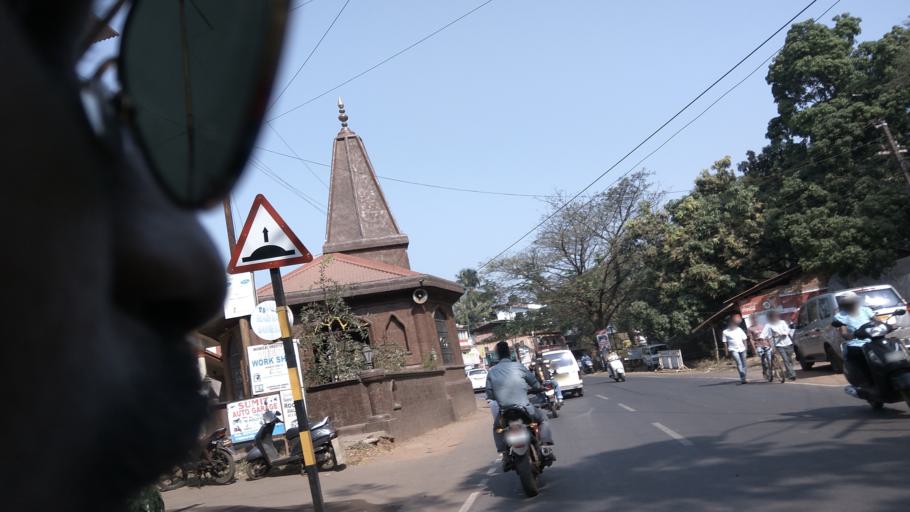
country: IN
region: Goa
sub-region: North Goa
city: Candolim
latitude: 15.5294
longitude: 73.7649
